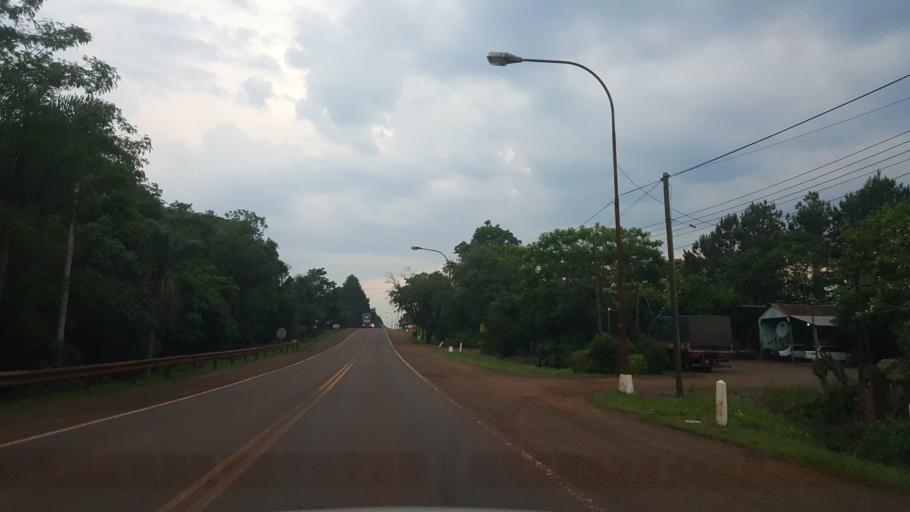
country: AR
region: Misiones
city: Gobernador Roca
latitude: -27.1828
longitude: -55.4609
